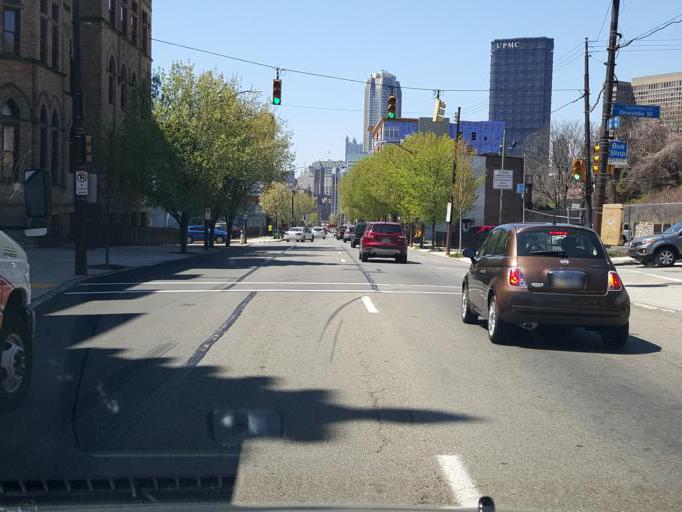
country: US
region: Pennsylvania
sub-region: Allegheny County
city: Pittsburgh
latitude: 40.4384
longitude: -79.9805
